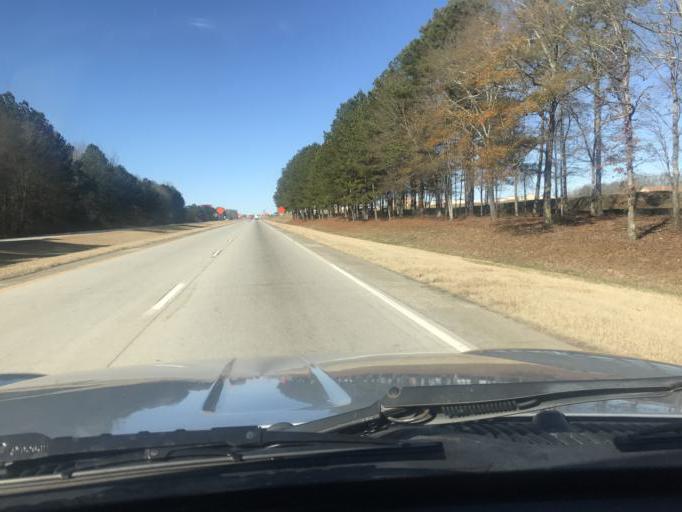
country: US
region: Georgia
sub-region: Barrow County
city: Russell
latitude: 33.9391
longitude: -83.7342
